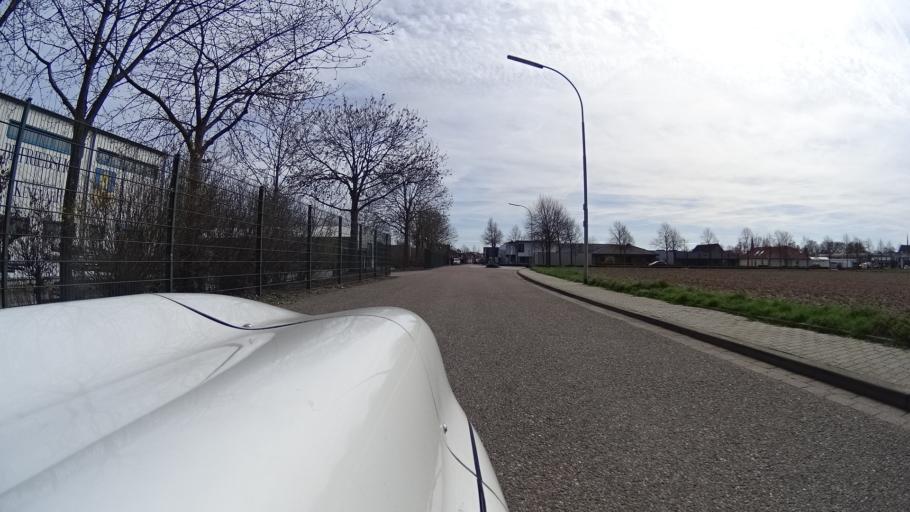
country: DE
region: North Rhine-Westphalia
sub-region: Regierungsbezirk Dusseldorf
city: Kevelaer
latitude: 51.5907
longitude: 6.2477
